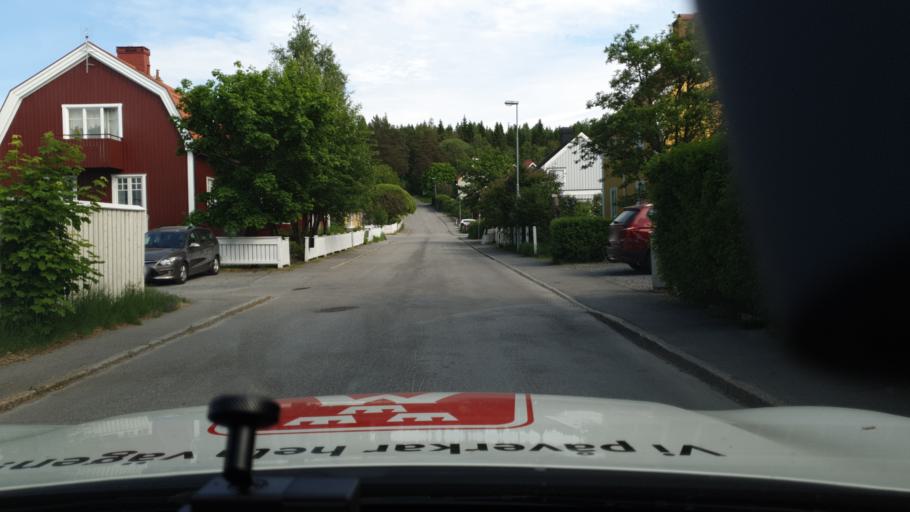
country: SE
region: Vaesterbotten
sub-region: Umea Kommun
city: Umea
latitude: 63.8380
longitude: 20.2835
